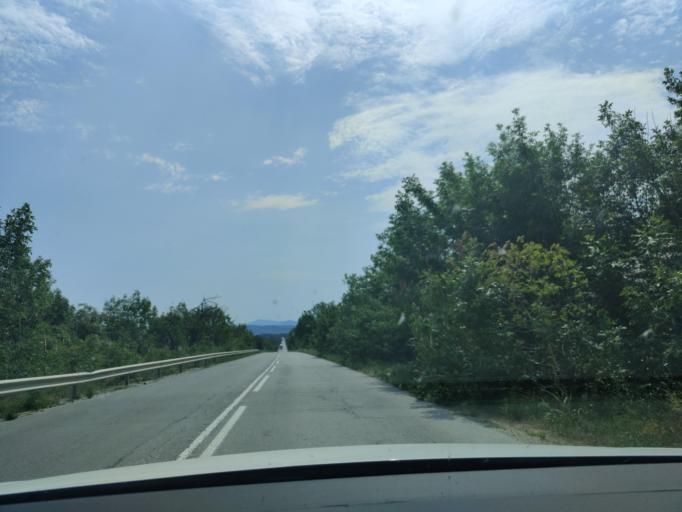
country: BG
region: Vidin
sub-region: Obshtina Ruzhintsi
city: Ruzhintsi
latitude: 43.5855
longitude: 22.8641
